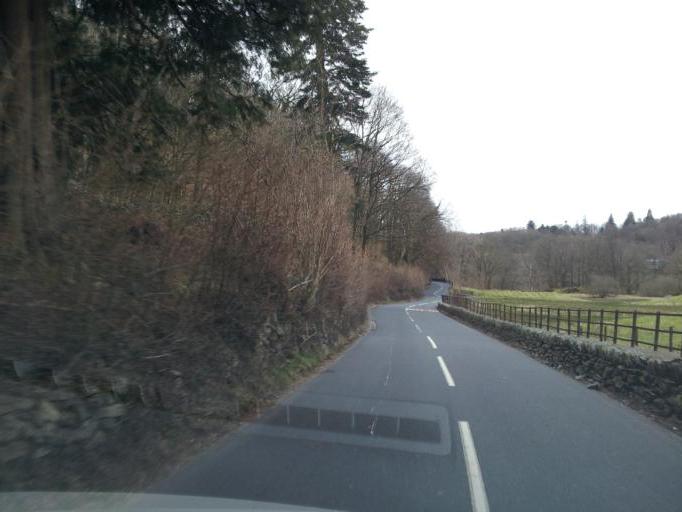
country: GB
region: England
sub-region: Cumbria
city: Ambleside
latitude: 54.4243
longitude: -3.0036
